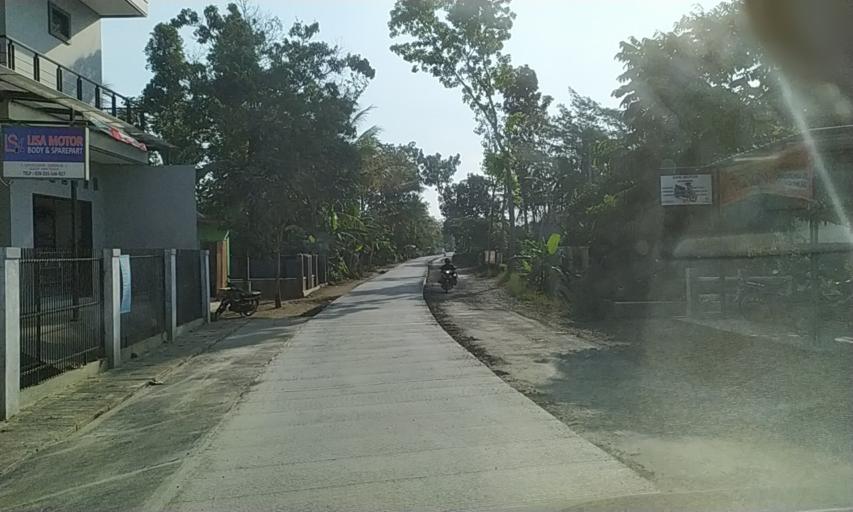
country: ID
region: Central Java
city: Kesugihan
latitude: -7.6234
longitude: 109.1028
